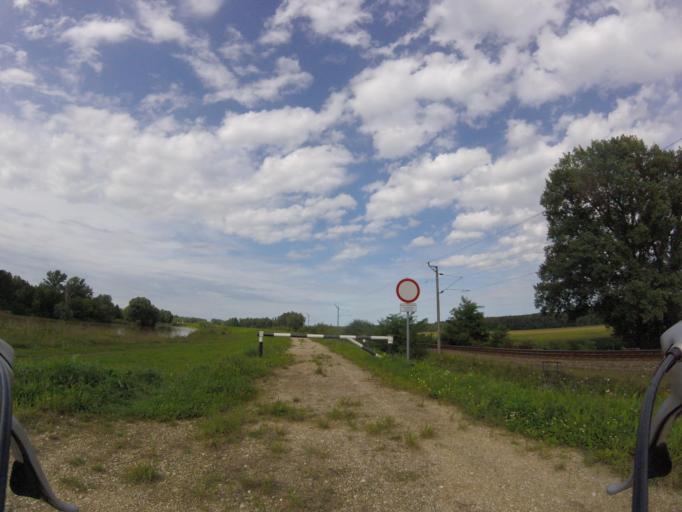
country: HU
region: Zala
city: Murakeresztur
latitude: 46.3320
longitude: 16.8805
